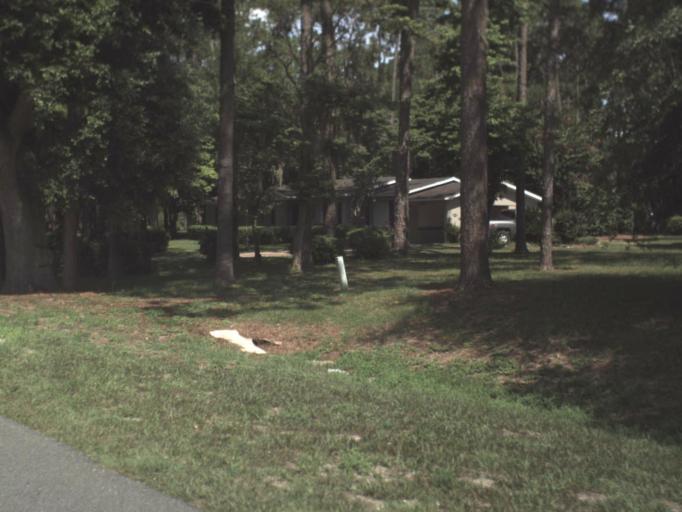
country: US
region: Florida
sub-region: Alachua County
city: Alachua
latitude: 29.8400
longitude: -82.3698
